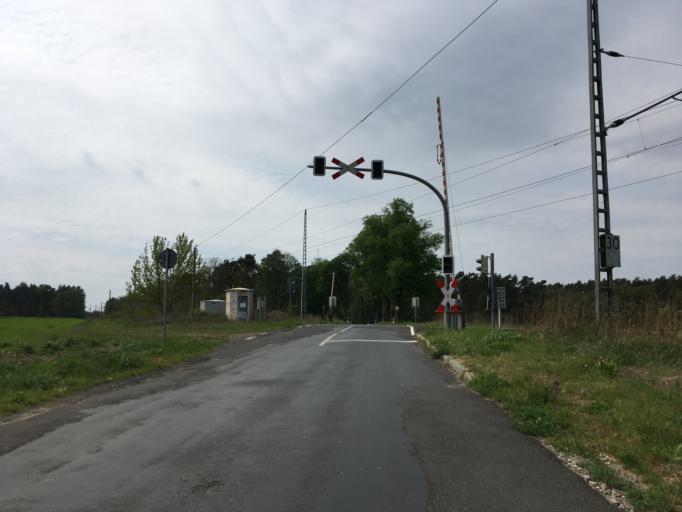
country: DE
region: Brandenburg
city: Rudnitz
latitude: 52.7319
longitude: 13.6512
